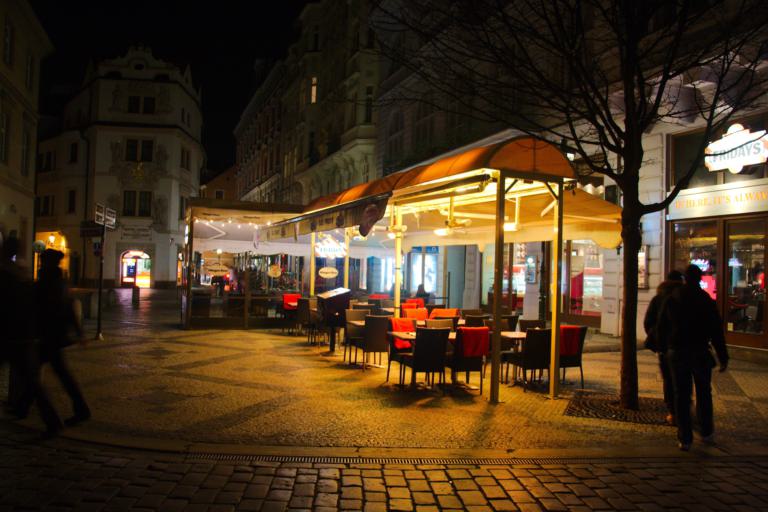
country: CZ
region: Praha
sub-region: Praha 1
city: Stare Mesto
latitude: 50.0863
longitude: 14.4151
